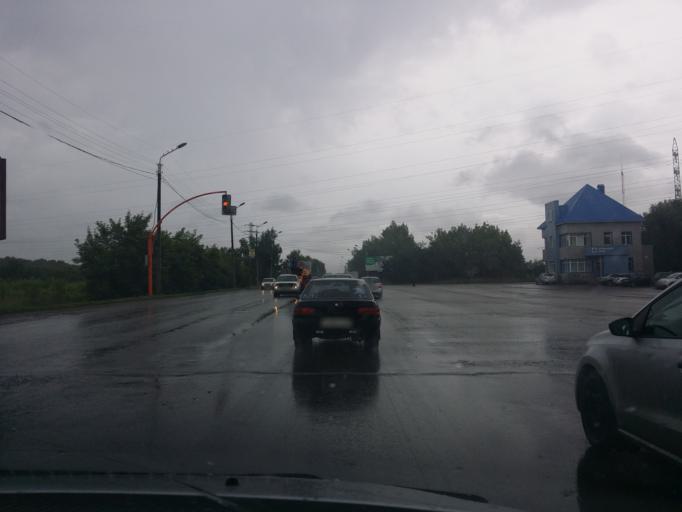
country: RU
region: Altai Krai
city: Novosilikatnyy
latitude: 53.3493
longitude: 83.6203
